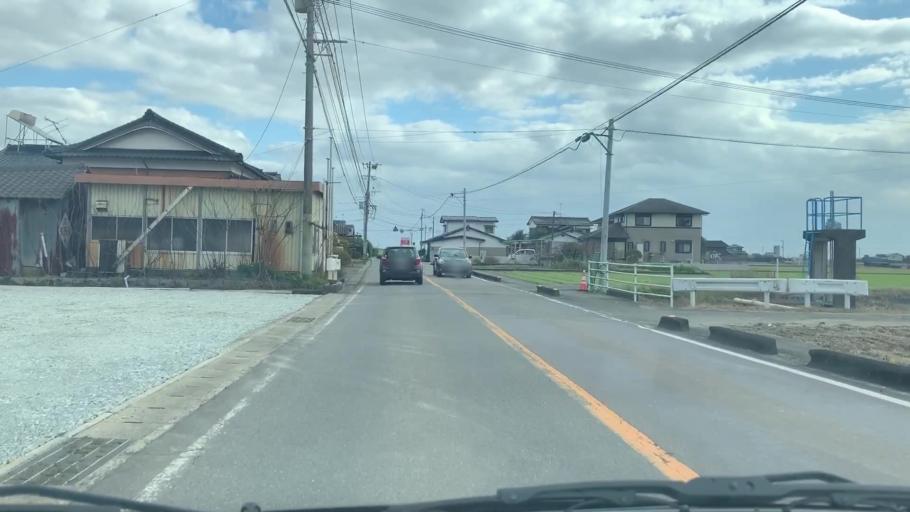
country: JP
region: Saga Prefecture
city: Takeocho-takeo
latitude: 33.2055
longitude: 130.0895
